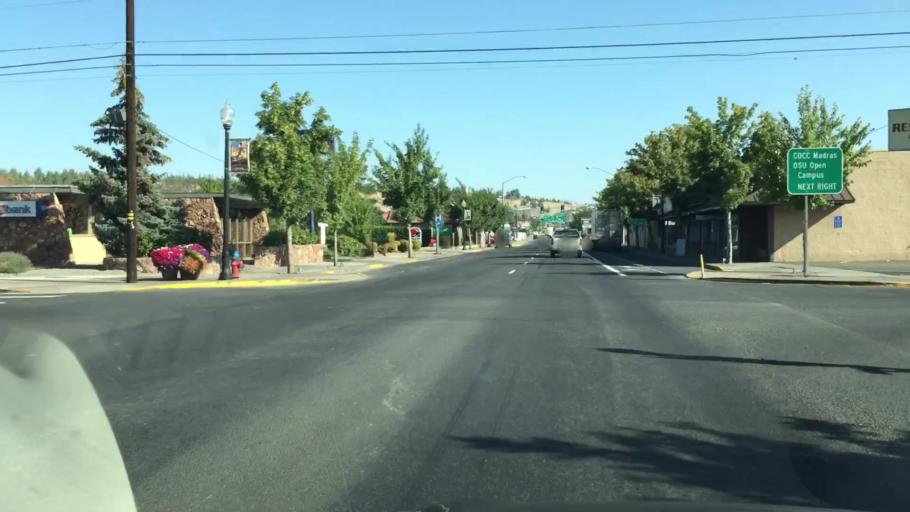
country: US
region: Oregon
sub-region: Jefferson County
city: Madras
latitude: 44.6346
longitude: -121.1296
